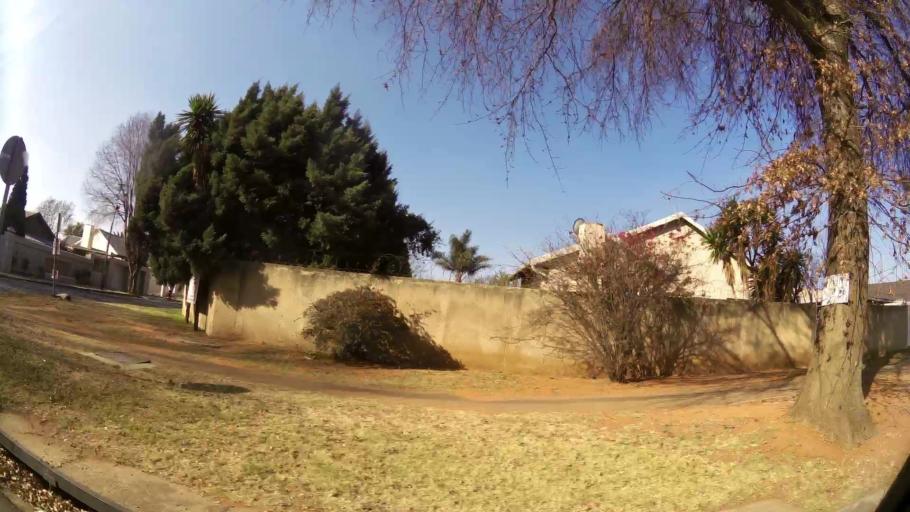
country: ZA
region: Gauteng
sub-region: City of Johannesburg Metropolitan Municipality
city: Johannesburg
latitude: -26.2558
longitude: 27.9971
